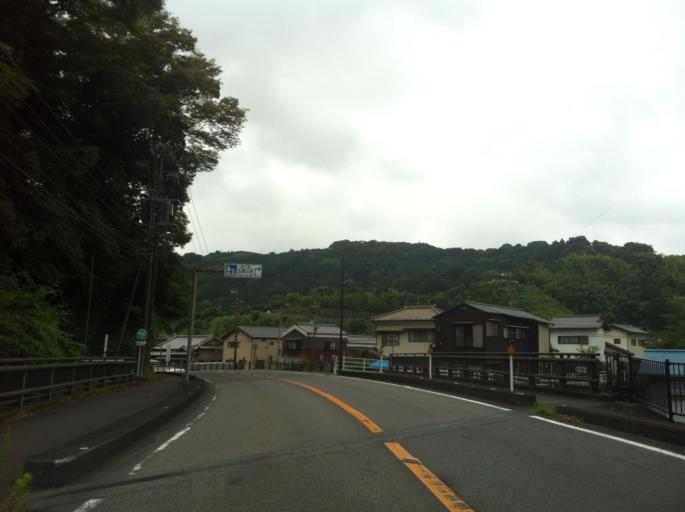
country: JP
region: Shizuoka
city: Fujieda
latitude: 34.9207
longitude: 138.2833
